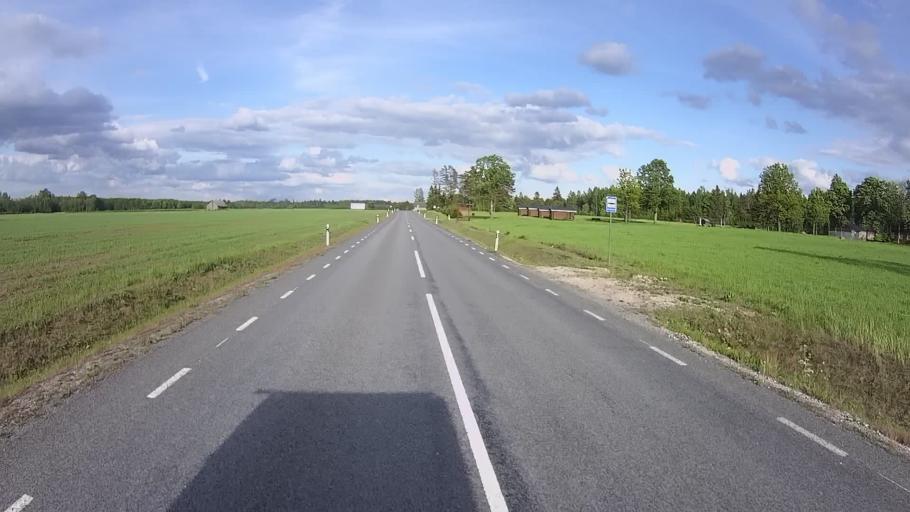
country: EE
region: Jogevamaa
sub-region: Mustvee linn
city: Mustvee
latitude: 59.0481
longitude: 27.0334
